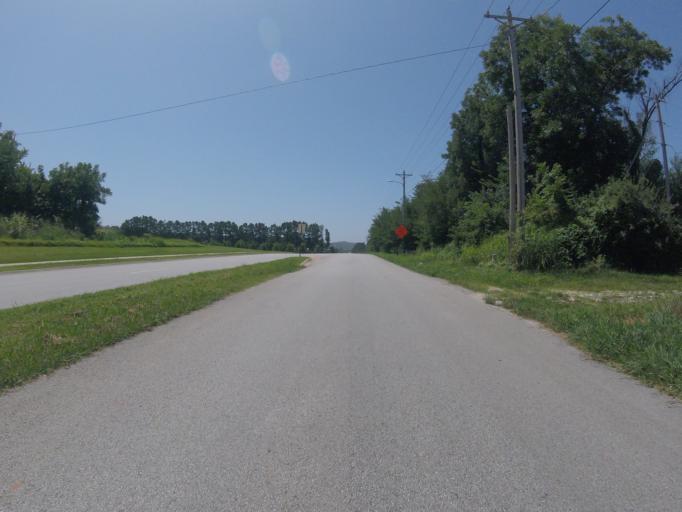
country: US
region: Arkansas
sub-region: Washington County
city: Farmington
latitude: 36.0824
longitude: -94.2174
